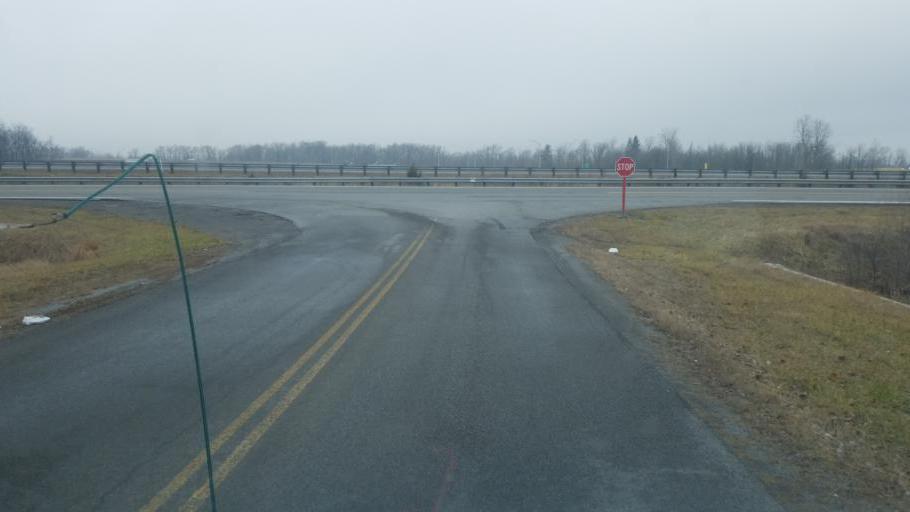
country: US
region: Ohio
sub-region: Champaign County
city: North Lewisburg
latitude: 40.3200
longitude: -83.5839
